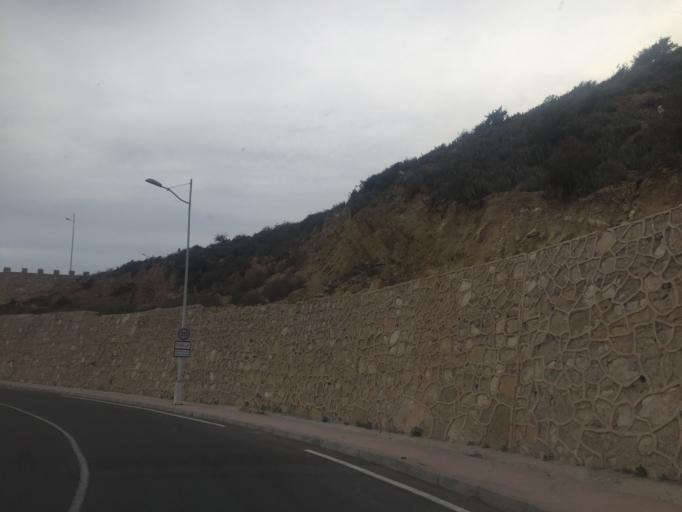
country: MA
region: Souss-Massa-Draa
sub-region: Agadir-Ida-ou-Tnan
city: Agadir
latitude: 30.4302
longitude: -9.6159
